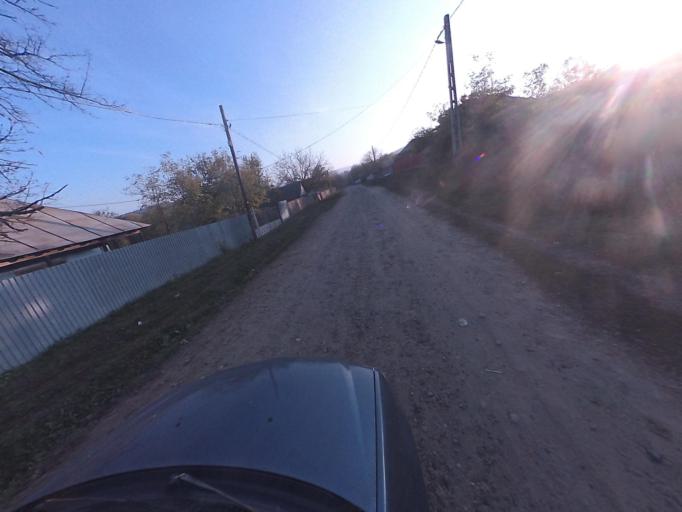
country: RO
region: Vaslui
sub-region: Comuna Bacesti
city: Bacesti
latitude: 46.8076
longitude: 27.2252
